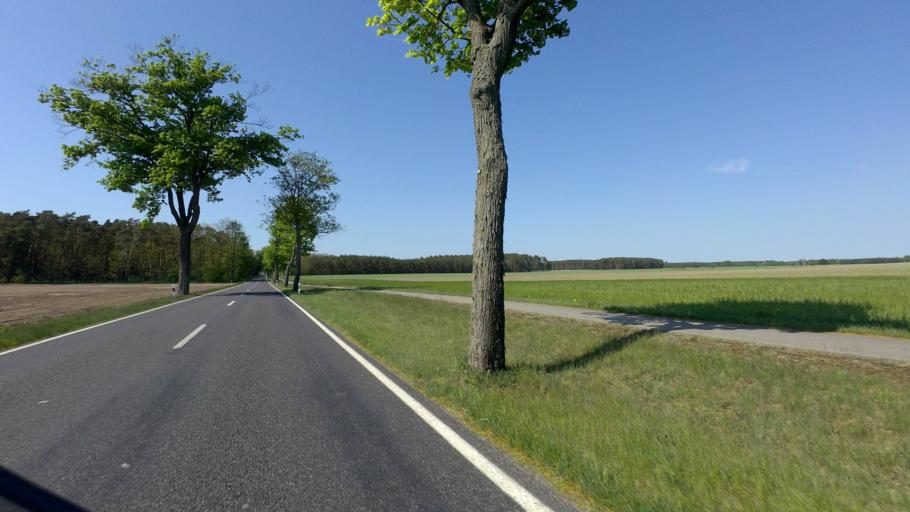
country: DE
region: Brandenburg
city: Neu Zauche
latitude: 52.0090
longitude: 14.0505
